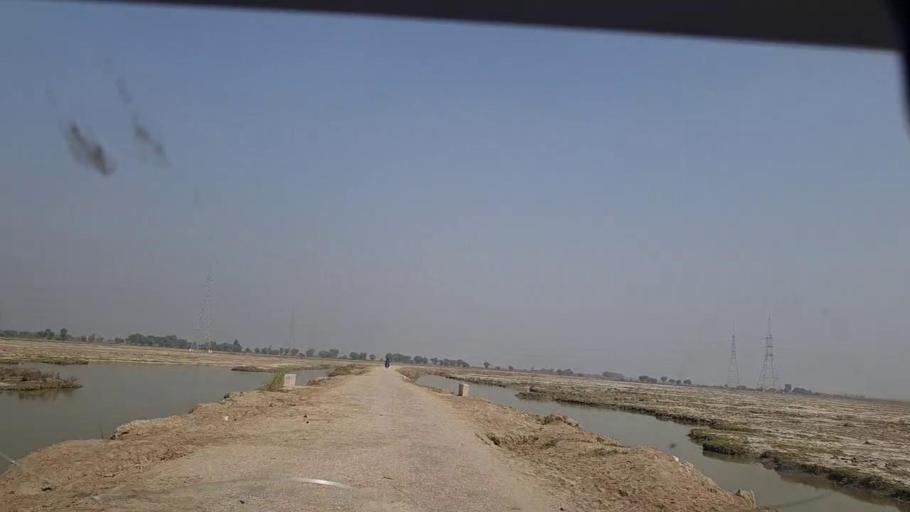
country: PK
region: Sindh
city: Shikarpur
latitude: 28.0335
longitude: 68.6298
